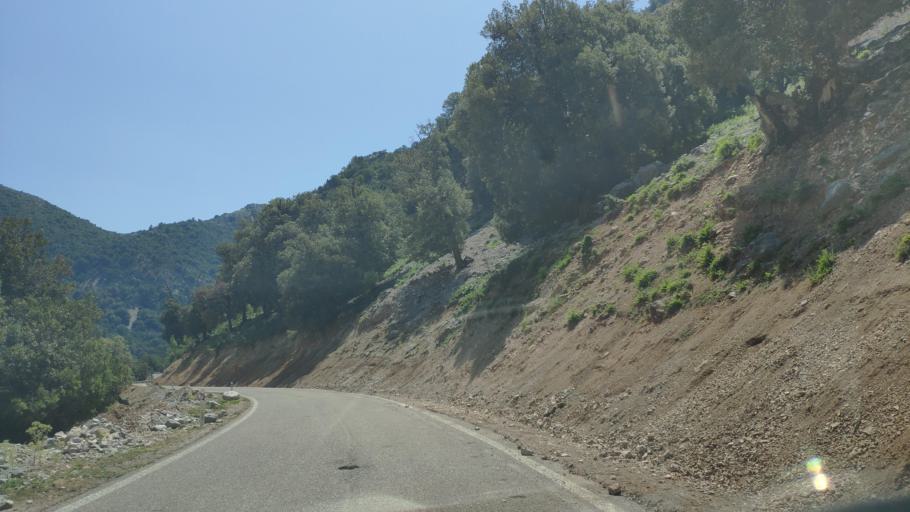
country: GR
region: West Greece
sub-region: Nomos Aitolias kai Akarnanias
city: Krikellos
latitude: 39.0183
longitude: 21.3477
